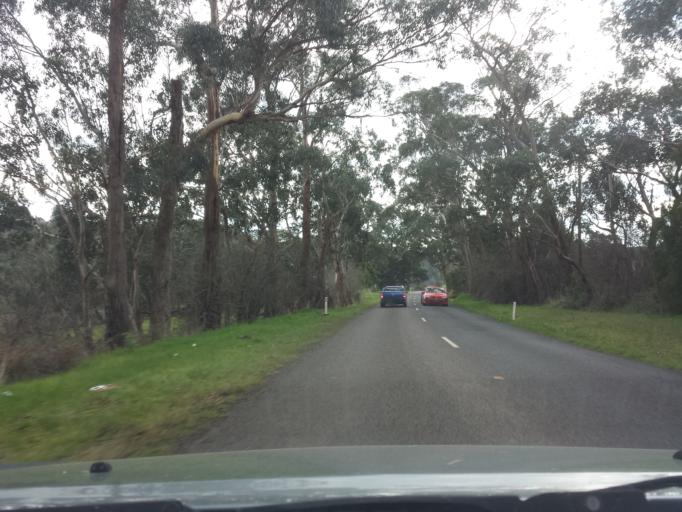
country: AU
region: Victoria
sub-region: Yarra Ranges
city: Woori Yallock
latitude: -37.7904
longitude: 145.4672
